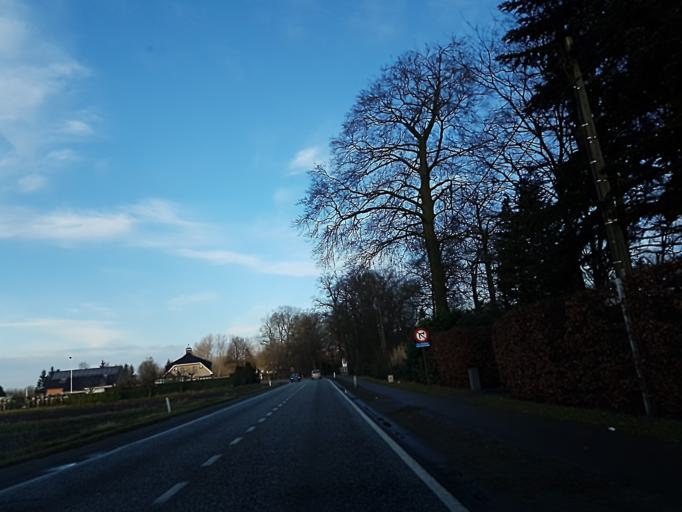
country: BE
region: Flanders
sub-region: Provincie Antwerpen
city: Ravels
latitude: 51.3516
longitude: 4.9843
